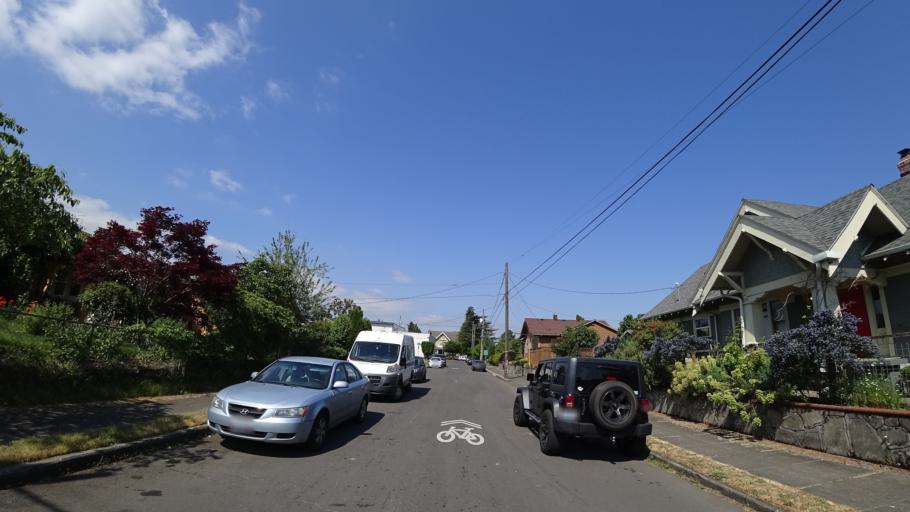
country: US
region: Oregon
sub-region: Multnomah County
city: Portland
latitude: 45.5682
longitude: -122.6595
